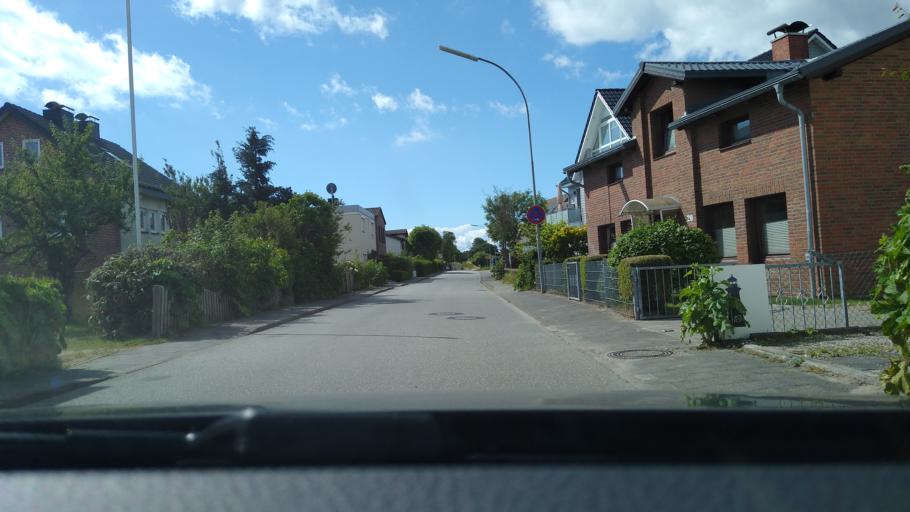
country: DE
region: Schleswig-Holstein
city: Dahme
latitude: 54.2174
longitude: 11.0895
